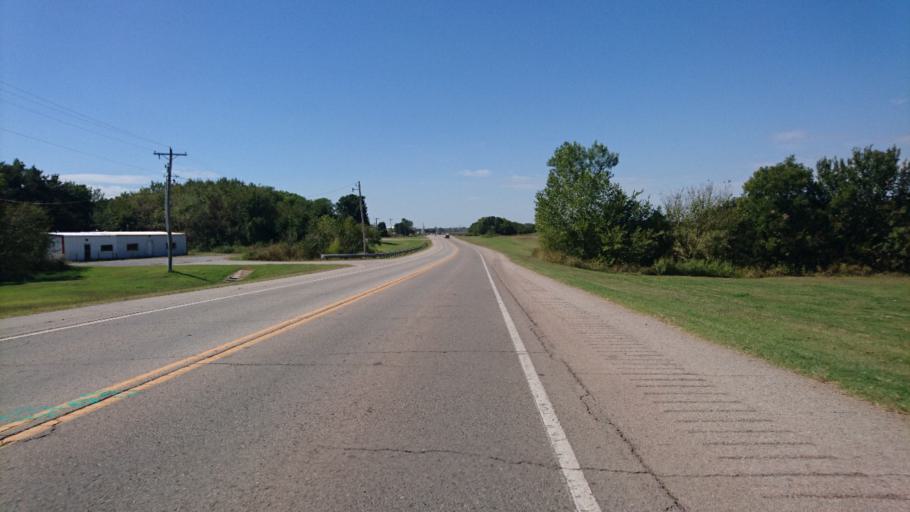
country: US
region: Oklahoma
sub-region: Oklahoma County
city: Jones
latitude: 35.6617
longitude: -97.3275
